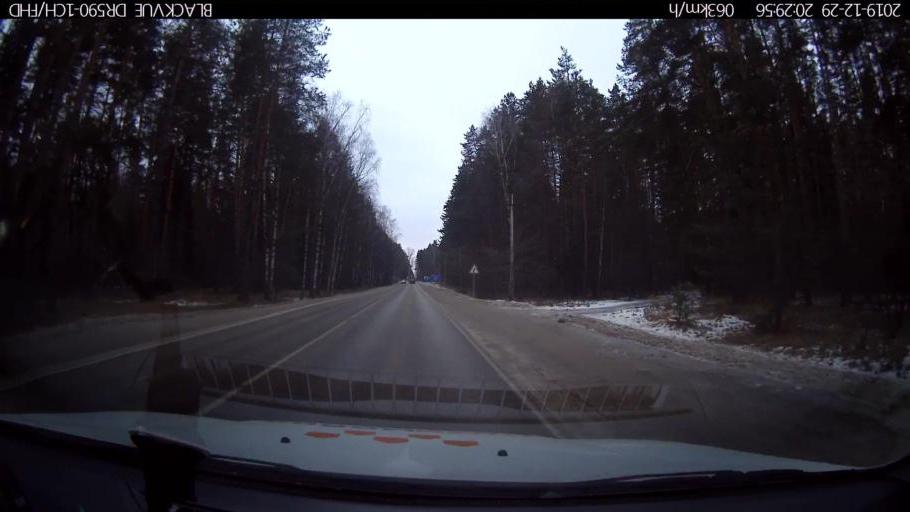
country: RU
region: Nizjnij Novgorod
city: Afonino
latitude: 56.1770
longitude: 44.0986
